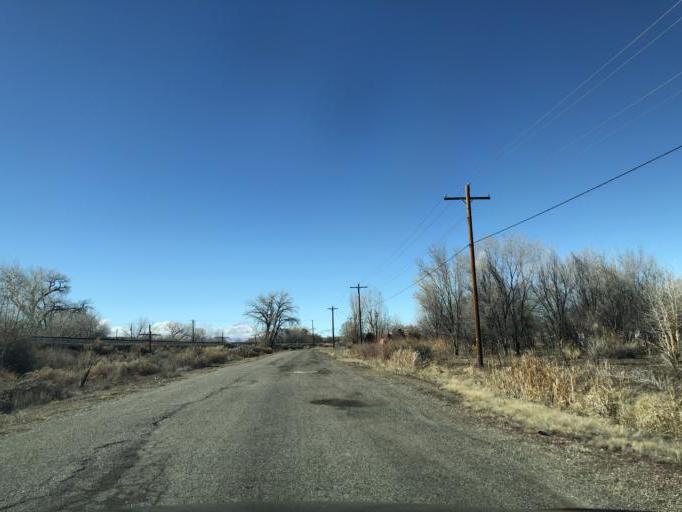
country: US
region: Utah
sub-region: Carbon County
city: East Carbon City
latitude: 38.9861
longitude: -110.1549
